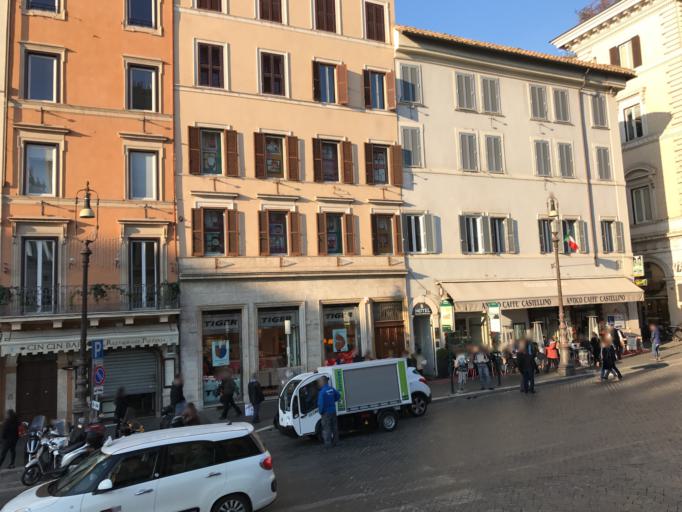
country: IT
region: Latium
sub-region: Citta metropolitana di Roma Capitale
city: Rome
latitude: 41.8967
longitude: 12.4826
